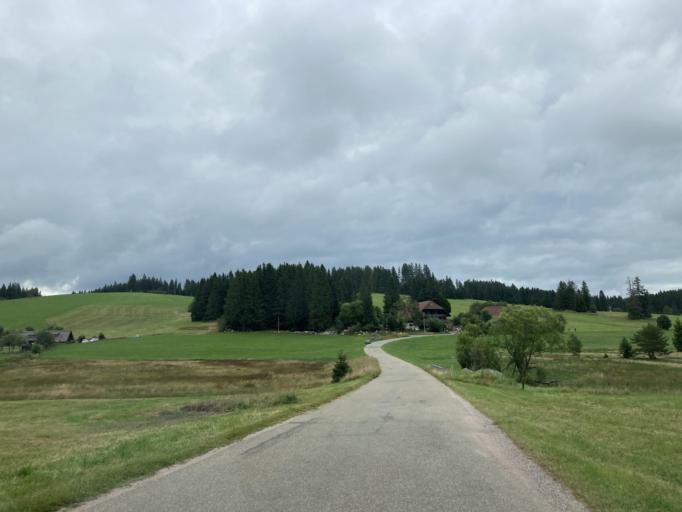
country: DE
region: Baden-Wuerttemberg
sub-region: Freiburg Region
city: Schonwald im Schwarzwald
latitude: 48.1180
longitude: 8.1971
